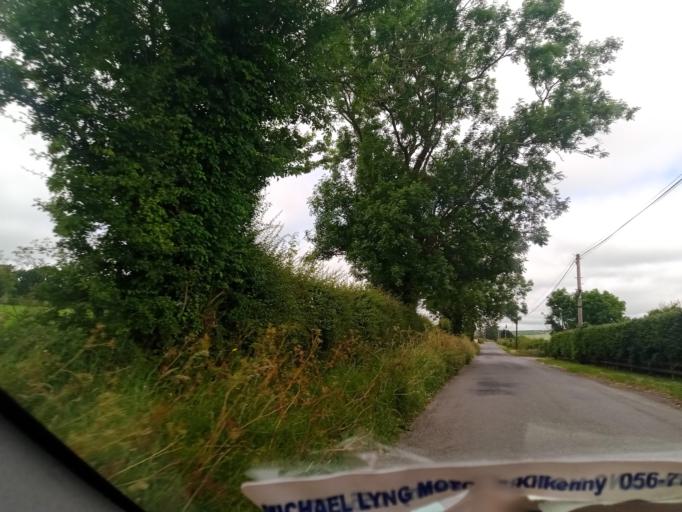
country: IE
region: Leinster
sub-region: Kilkenny
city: Ballyragget
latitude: 52.7549
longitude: -7.4450
